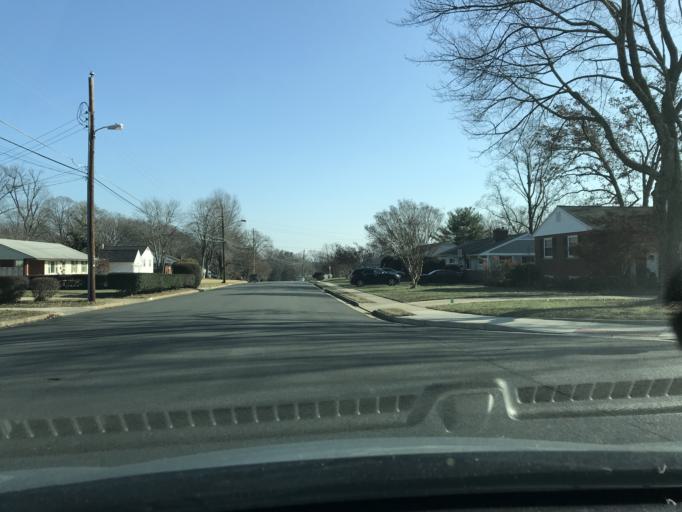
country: US
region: Virginia
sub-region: City of Fairfax
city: Fairfax
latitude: 38.8582
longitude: -77.3255
